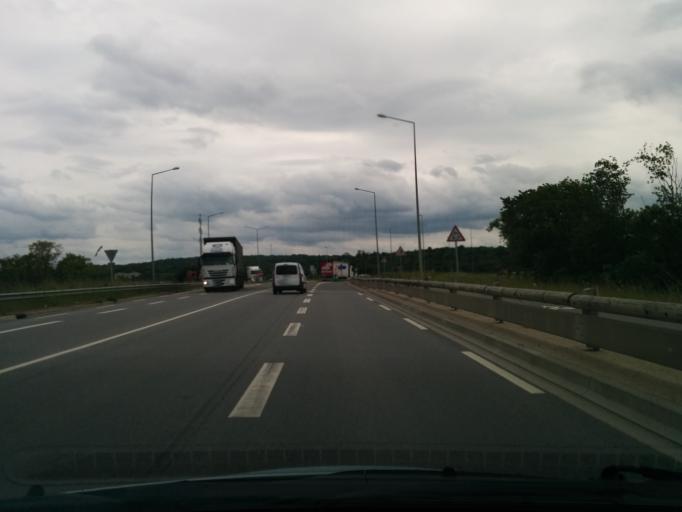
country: FR
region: Ile-de-France
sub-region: Departement des Yvelines
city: Flins-sur-Seine
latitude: 48.9714
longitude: 1.8636
